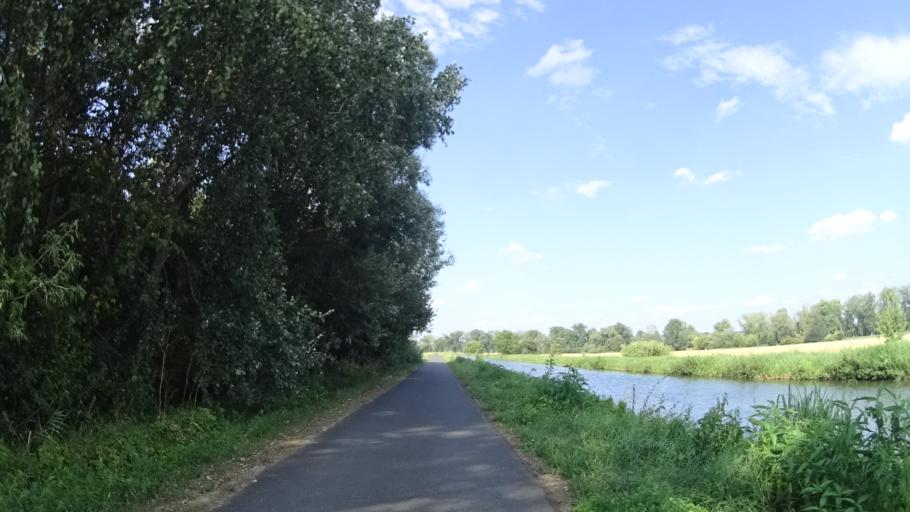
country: CZ
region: Zlin
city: Babice
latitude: 49.1260
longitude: 17.4939
